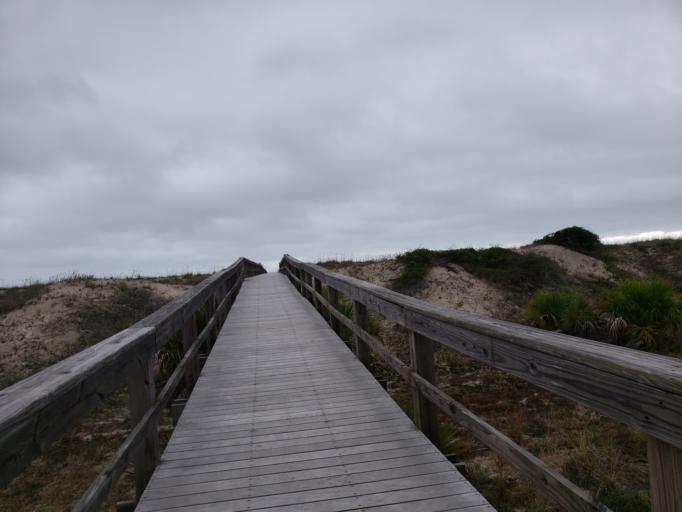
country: US
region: Georgia
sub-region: Chatham County
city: Tybee Island
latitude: 32.0030
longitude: -80.8424
